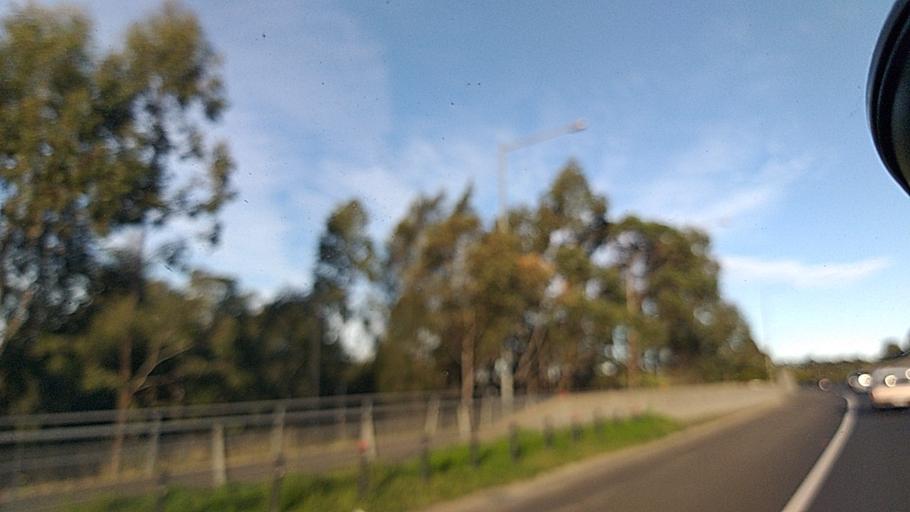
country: AU
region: New South Wales
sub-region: Blacktown
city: Doonside
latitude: -33.7694
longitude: 150.8473
